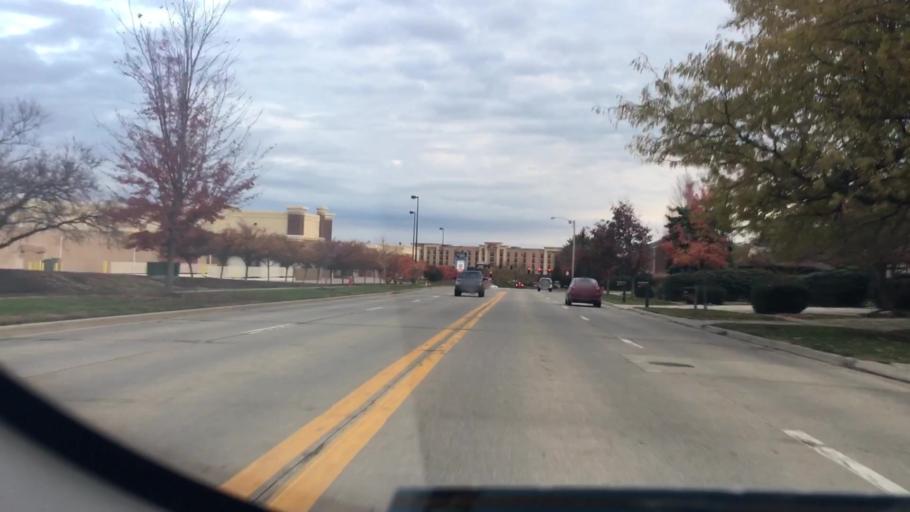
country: US
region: Illinois
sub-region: McLean County
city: Normal
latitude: 40.5070
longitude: -88.9595
